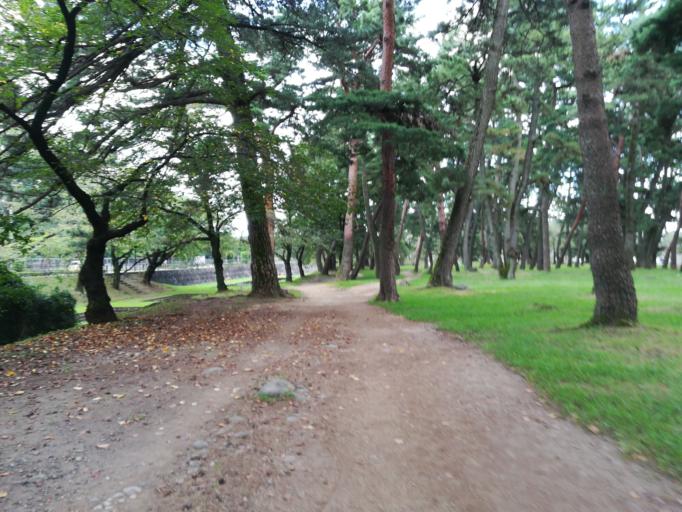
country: JP
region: Gunma
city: Maebashi-shi
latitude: 36.4188
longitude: 139.0513
